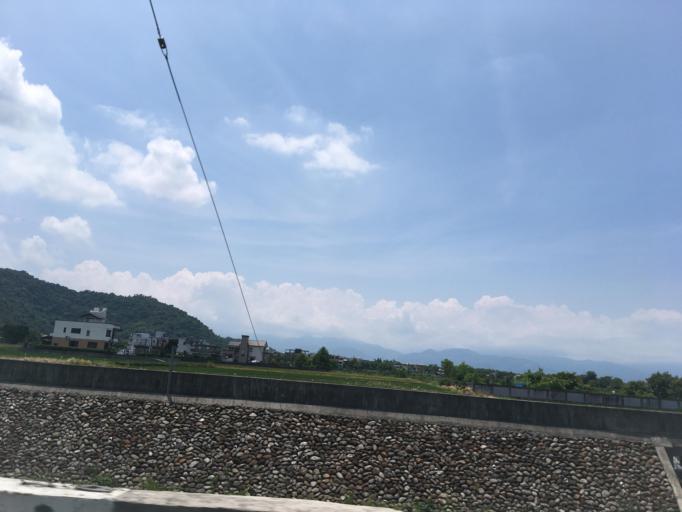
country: TW
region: Taiwan
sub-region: Yilan
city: Yilan
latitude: 24.6408
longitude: 121.7577
